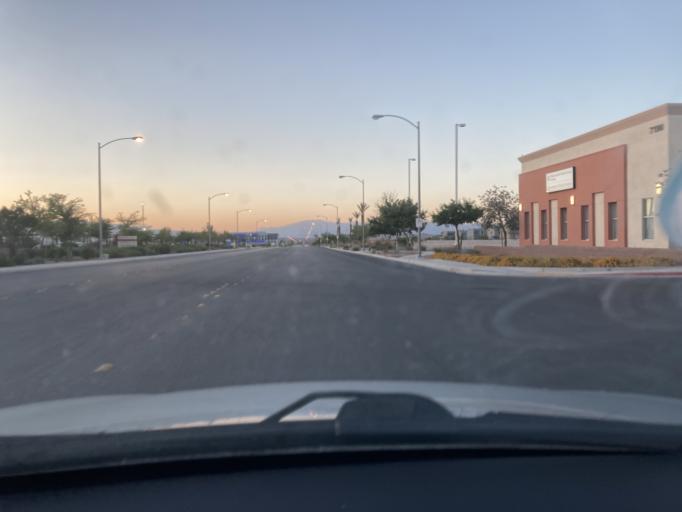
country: US
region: Nevada
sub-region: Clark County
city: Enterprise
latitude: 36.0573
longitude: -115.2701
